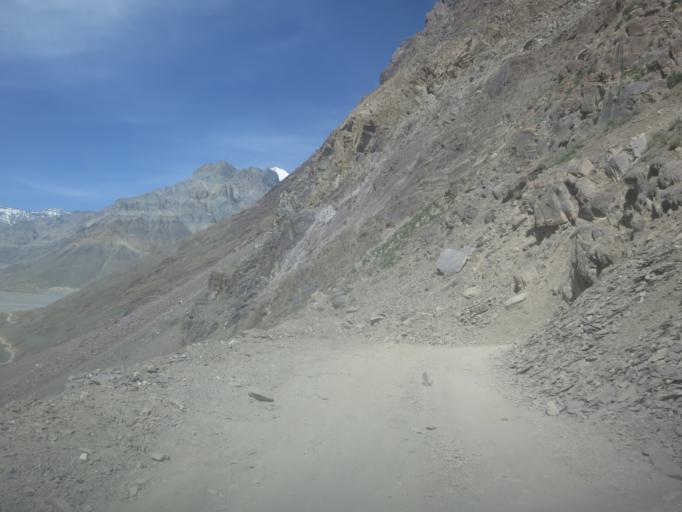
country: IN
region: Himachal Pradesh
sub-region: Kulu
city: Manali
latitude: 32.4381
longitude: 77.6839
